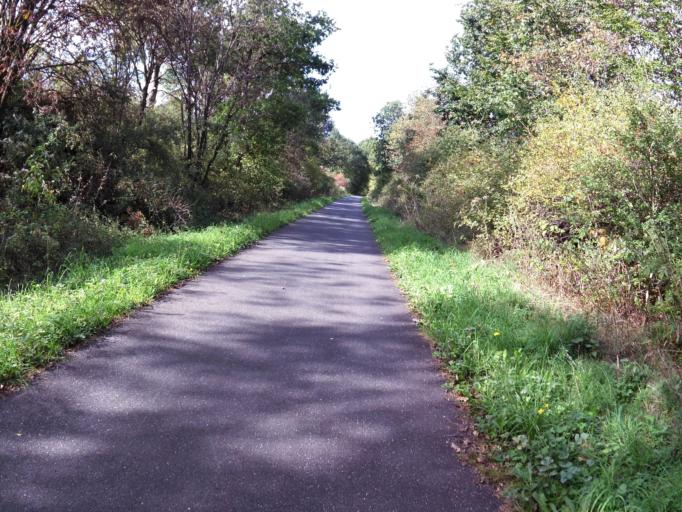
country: DE
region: Rheinland-Pfalz
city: Bleialf
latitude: 50.2197
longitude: 6.2696
